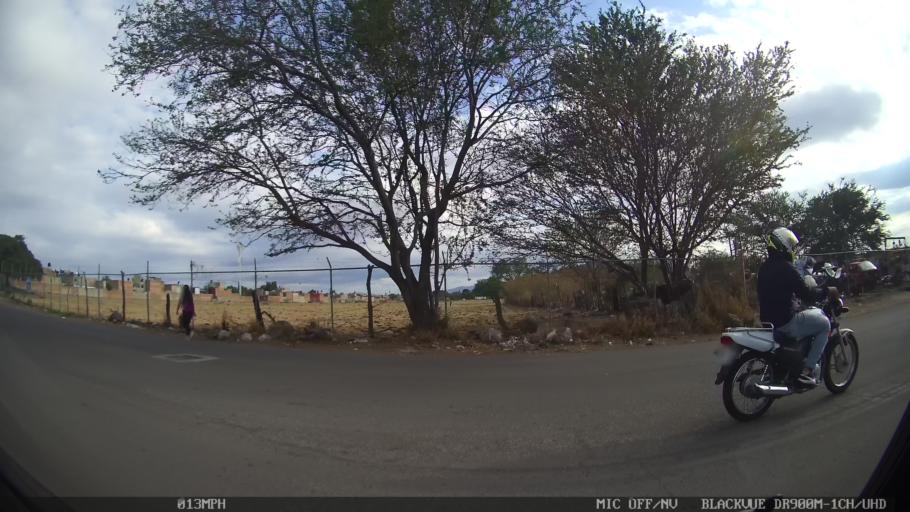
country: MX
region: Jalisco
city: Tlaquepaque
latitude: 20.6775
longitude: -103.2549
